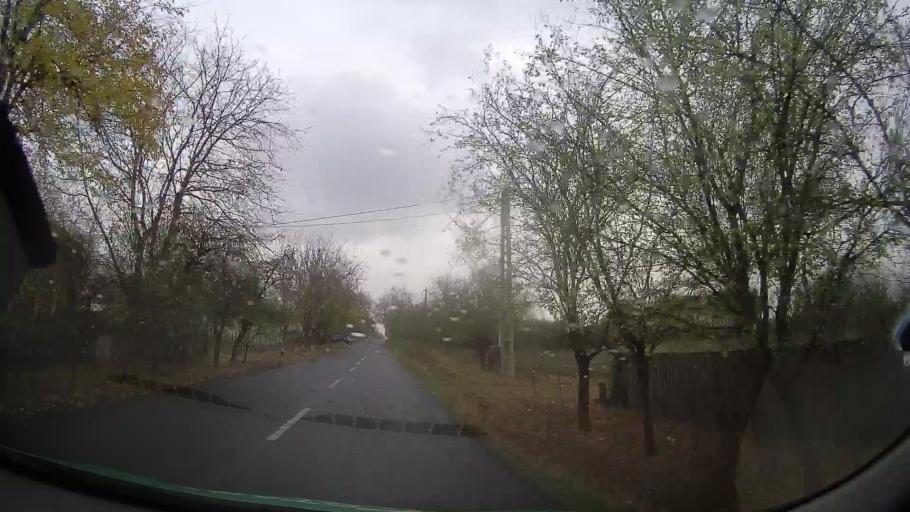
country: RO
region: Ialomita
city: Brazii
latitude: 44.7840
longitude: 26.3193
